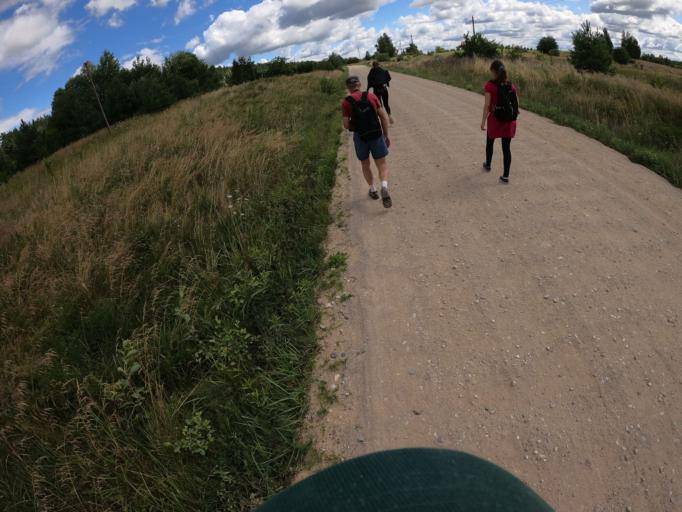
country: LT
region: Alytaus apskritis
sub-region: Alytus
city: Alytus
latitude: 54.3331
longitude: 24.0831
